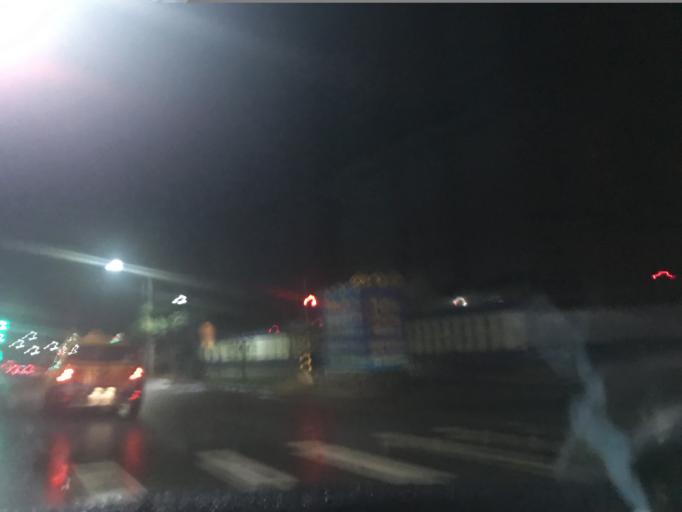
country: TW
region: Taiwan
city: Daxi
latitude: 24.9248
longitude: 121.2811
